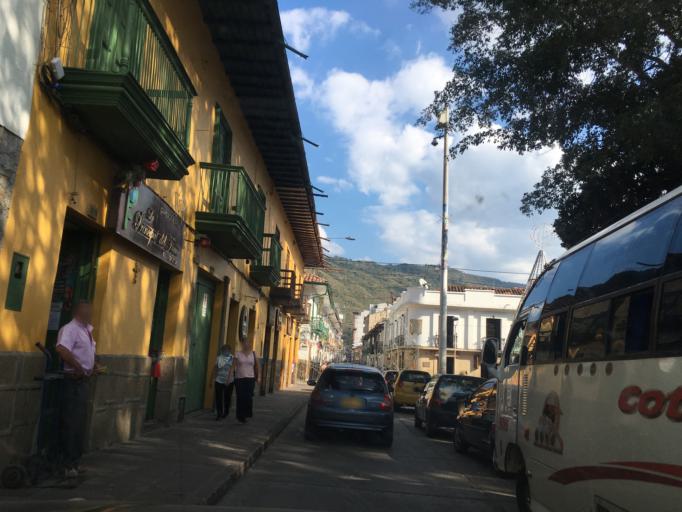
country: CO
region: Santander
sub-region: San Gil
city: San Gil
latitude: 6.5552
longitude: -73.1333
